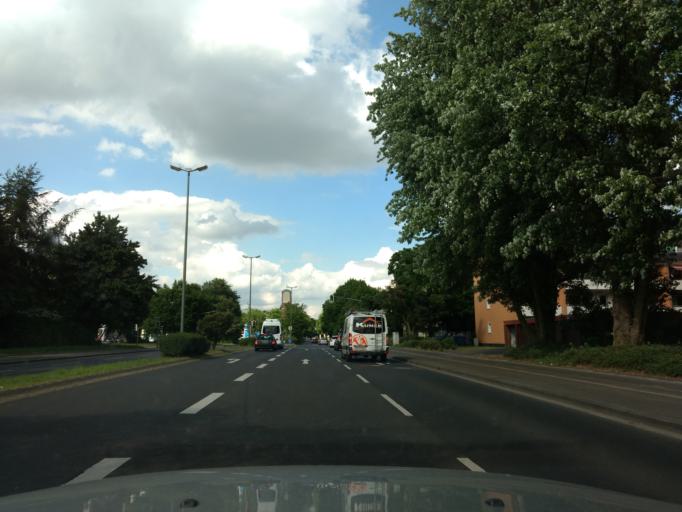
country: DE
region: North Rhine-Westphalia
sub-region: Regierungsbezirk Dusseldorf
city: Neuss
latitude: 51.2056
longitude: 6.6698
